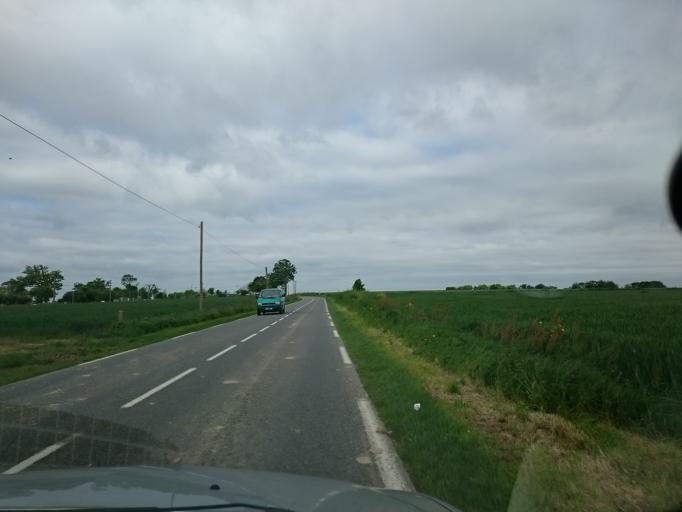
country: FR
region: Lower Normandy
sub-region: Departement de la Manche
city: Pontorson
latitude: 48.5531
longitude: -1.4266
